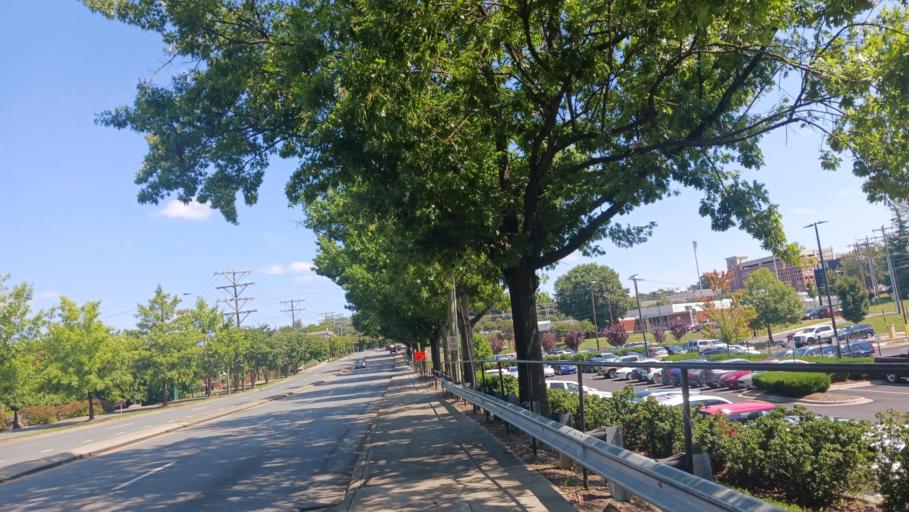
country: US
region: North Carolina
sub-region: Mecklenburg County
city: Charlotte
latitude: 35.2185
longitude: -80.8315
